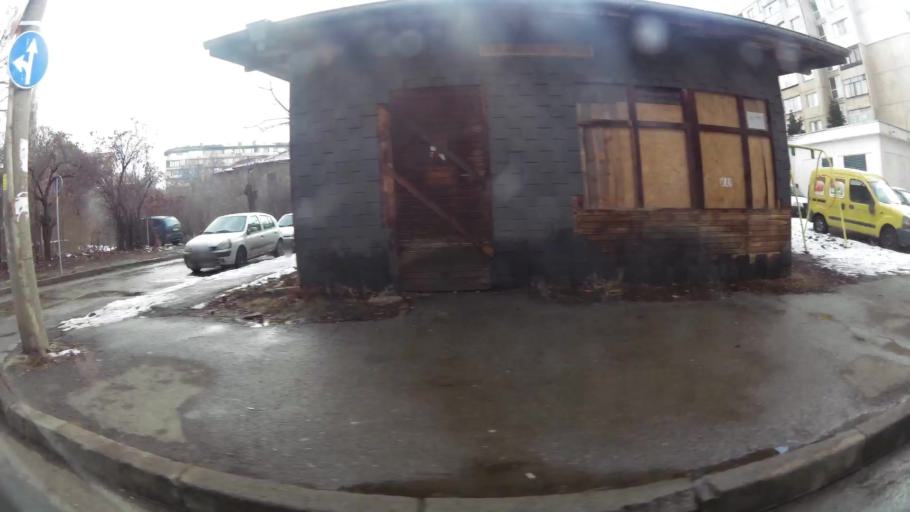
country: BG
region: Sofia-Capital
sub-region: Stolichna Obshtina
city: Sofia
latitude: 42.7009
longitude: 23.2882
